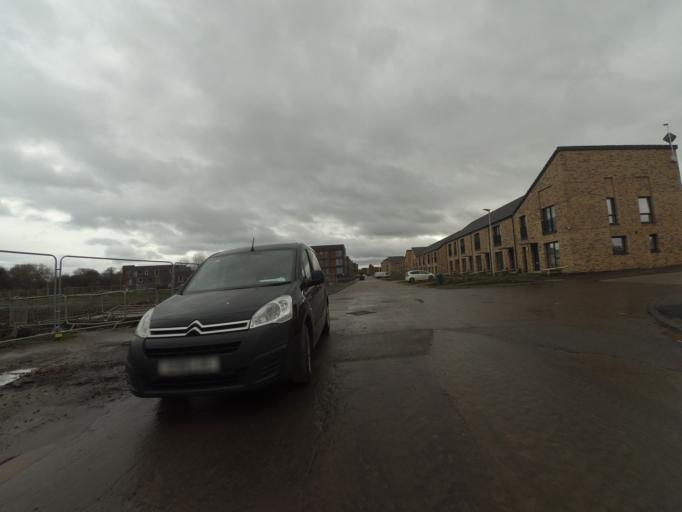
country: GB
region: Scotland
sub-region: West Lothian
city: Seafield
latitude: 55.9350
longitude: -3.1346
